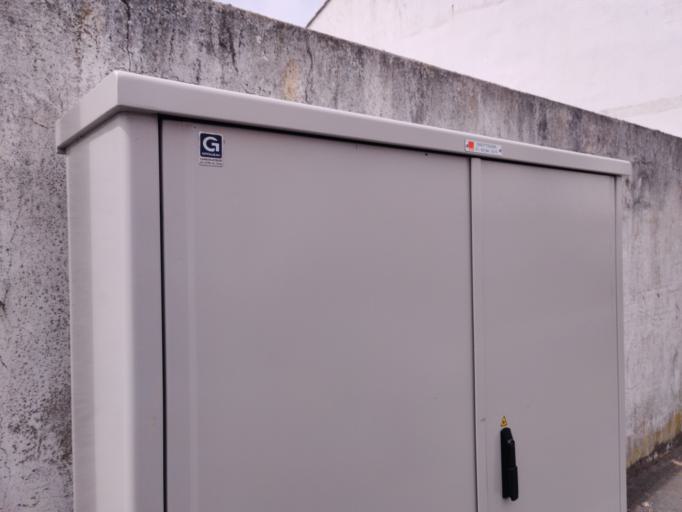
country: FR
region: Pays de la Loire
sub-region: Departement de la Vendee
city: Les Sables-d'Olonne
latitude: 46.4986
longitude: -1.7778
